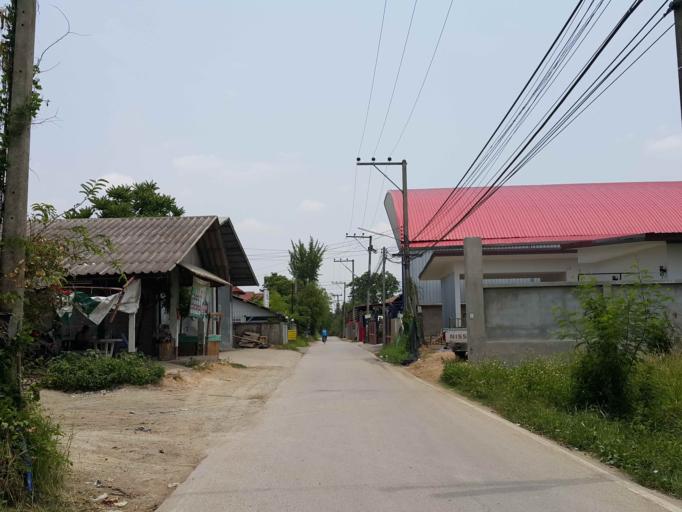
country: TH
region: Chiang Mai
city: Saraphi
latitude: 18.7531
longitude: 99.0357
